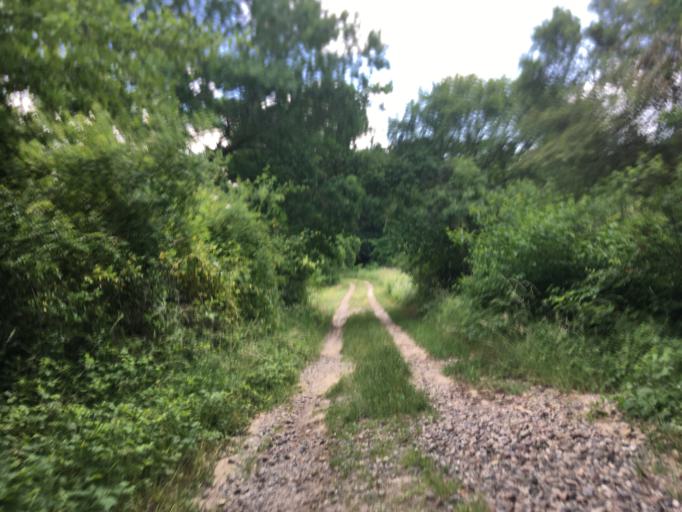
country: DE
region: Brandenburg
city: Buckow
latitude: 52.5812
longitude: 14.0609
